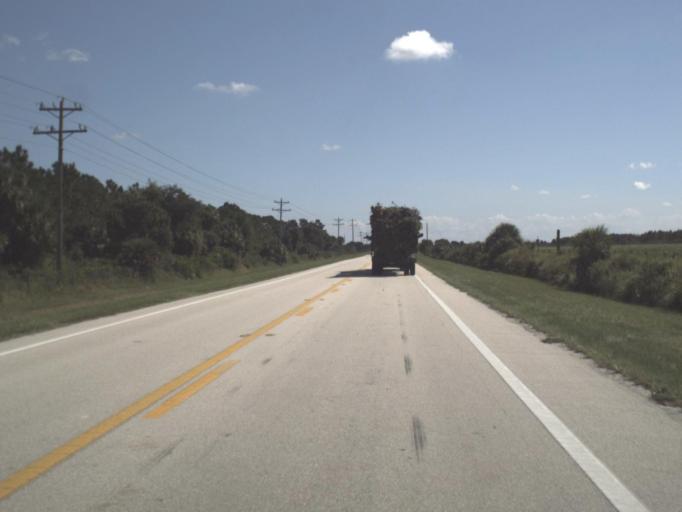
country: US
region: Florida
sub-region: Hendry County
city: Port LaBelle
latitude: 26.8124
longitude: -81.2743
